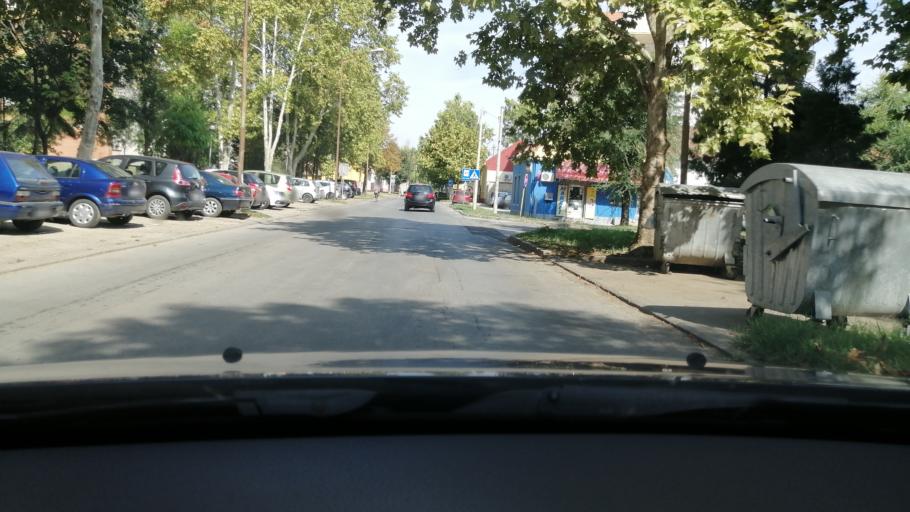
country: RS
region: Autonomna Pokrajina Vojvodina
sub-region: Srednjebanatski Okrug
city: Zrenjanin
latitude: 45.3840
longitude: 20.3783
